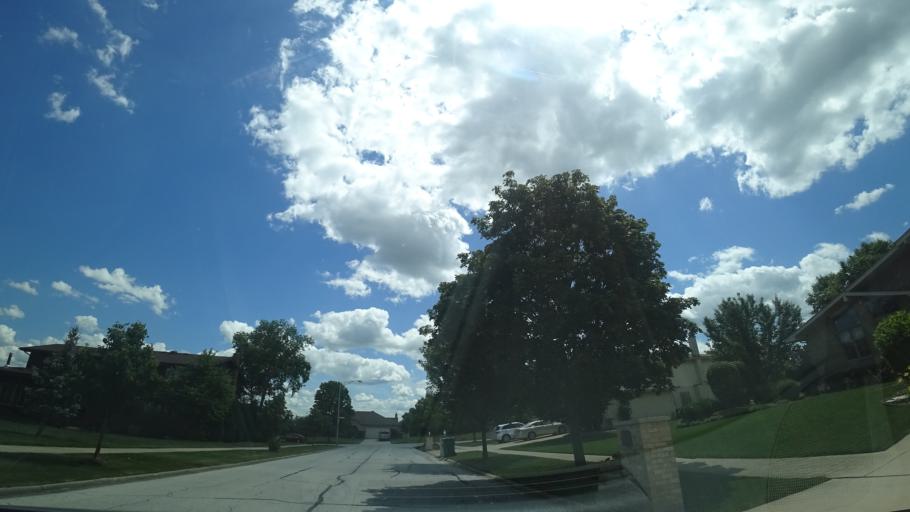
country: US
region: Illinois
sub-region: Will County
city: Homer Glen
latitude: 41.5737
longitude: -87.9089
